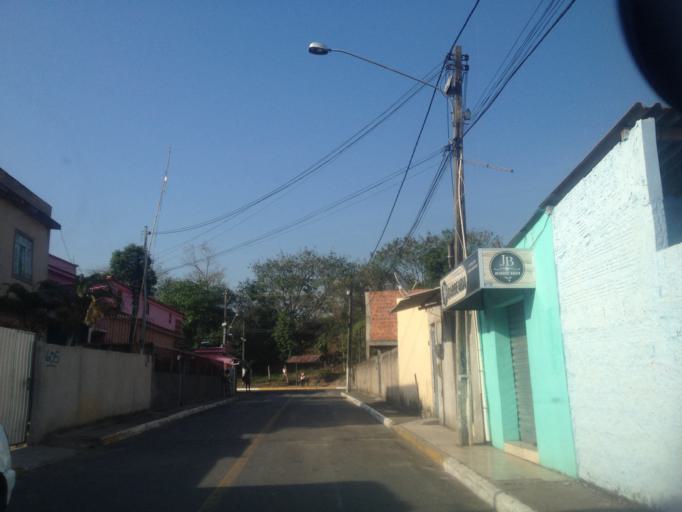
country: BR
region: Rio de Janeiro
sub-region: Porto Real
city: Porto Real
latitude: -22.4470
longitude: -44.3087
